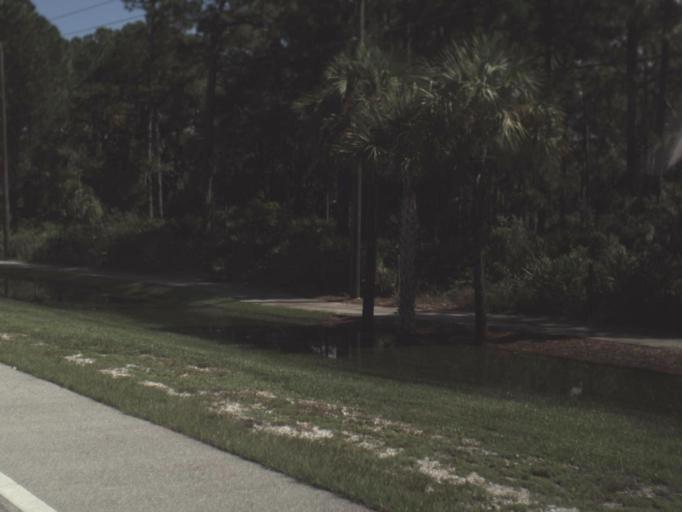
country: US
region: Florida
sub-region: Sarasota County
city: North Port
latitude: 27.0705
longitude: -82.1564
